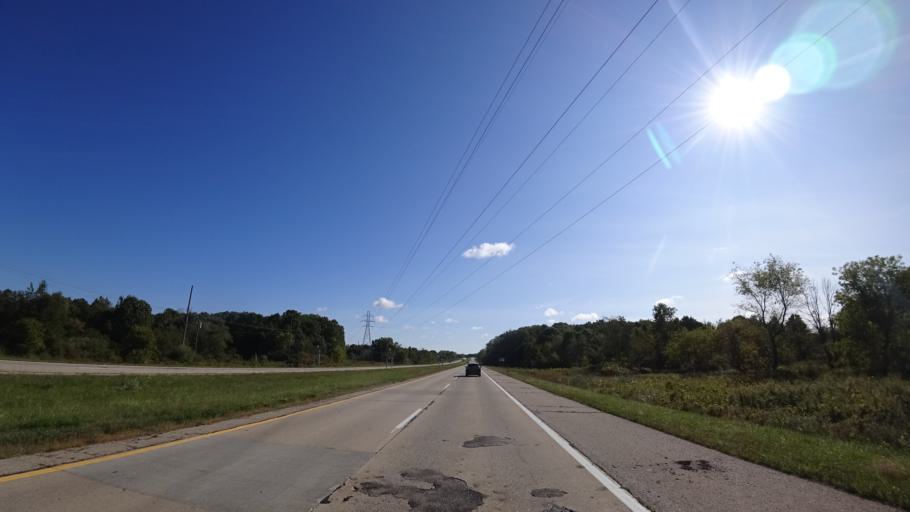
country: US
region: Michigan
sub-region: Berrien County
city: Benton Heights
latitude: 42.1190
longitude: -86.4070
